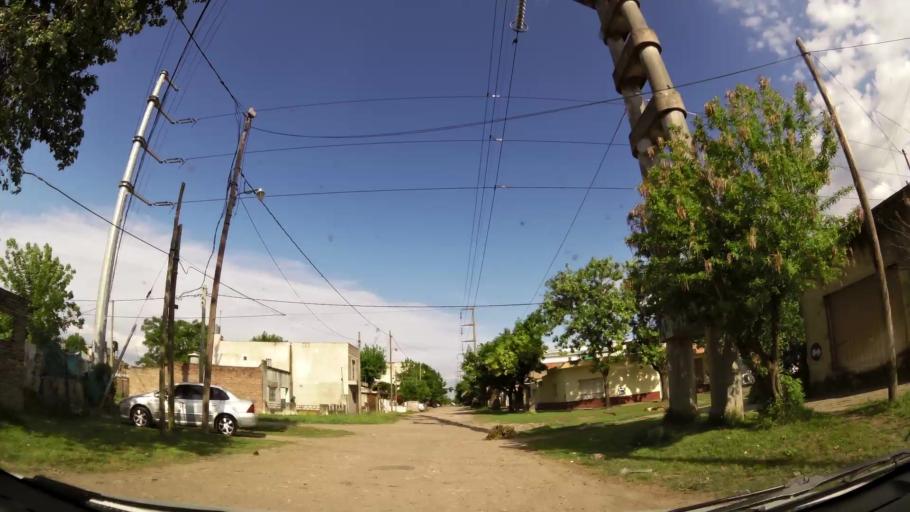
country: AR
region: Buenos Aires
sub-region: Partido de Merlo
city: Merlo
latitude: -34.6569
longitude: -58.7337
